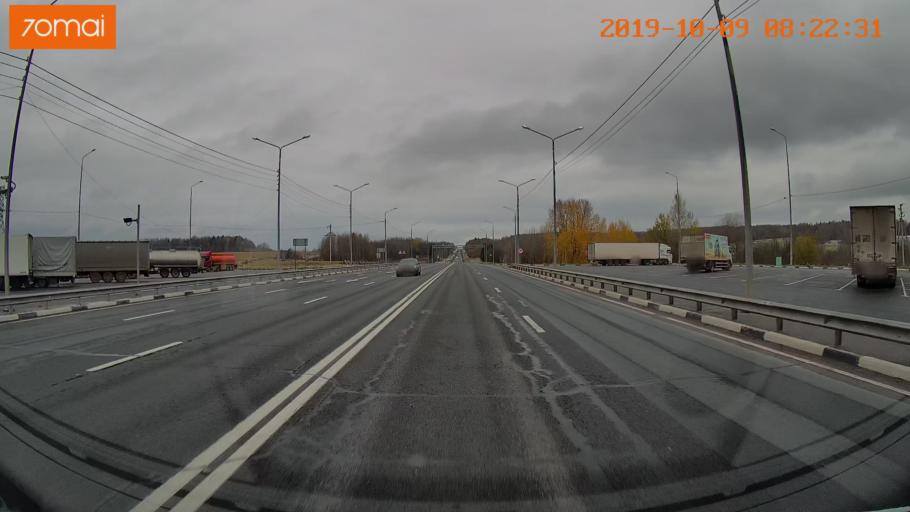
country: RU
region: Vologda
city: Gryazovets
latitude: 58.7423
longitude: 40.2888
